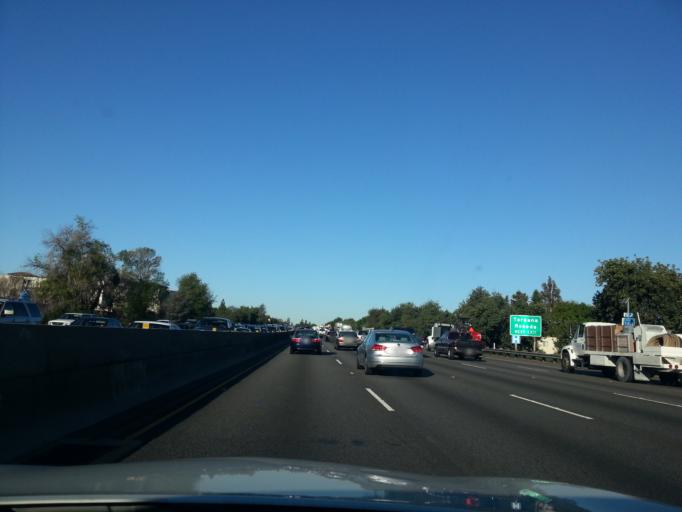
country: US
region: California
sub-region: Los Angeles County
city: Northridge
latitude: 34.1712
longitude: -118.5226
